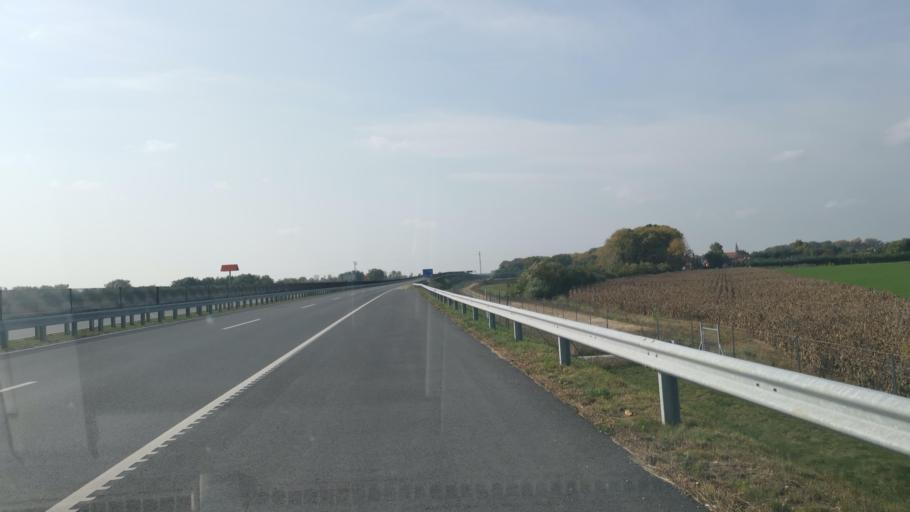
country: HU
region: Gyor-Moson-Sopron
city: Farad
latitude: 47.5875
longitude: 17.1841
